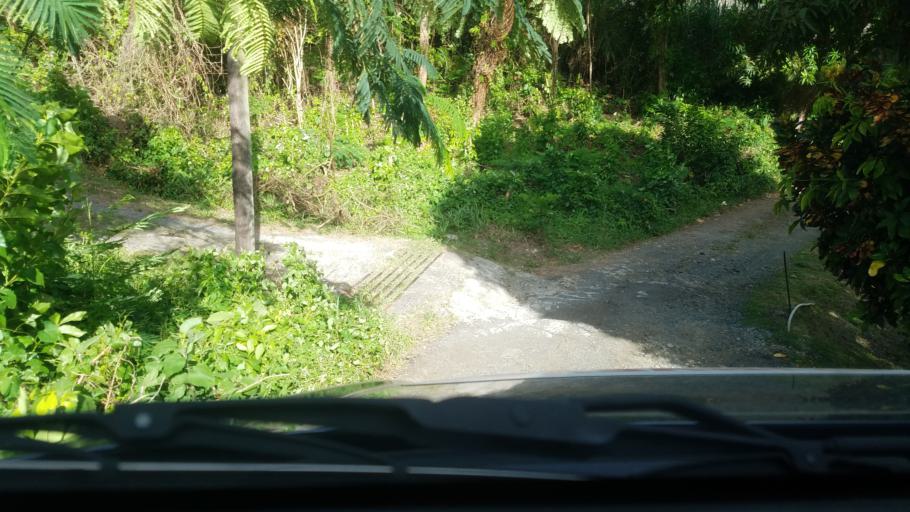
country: LC
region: Gros-Islet
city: Gros Islet
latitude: 14.0387
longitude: -60.9497
